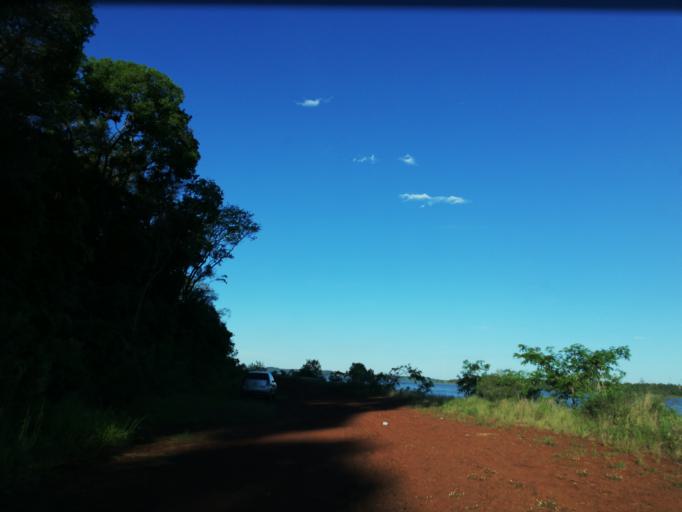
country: AR
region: Misiones
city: Garupa
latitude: -27.4604
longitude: -55.8146
